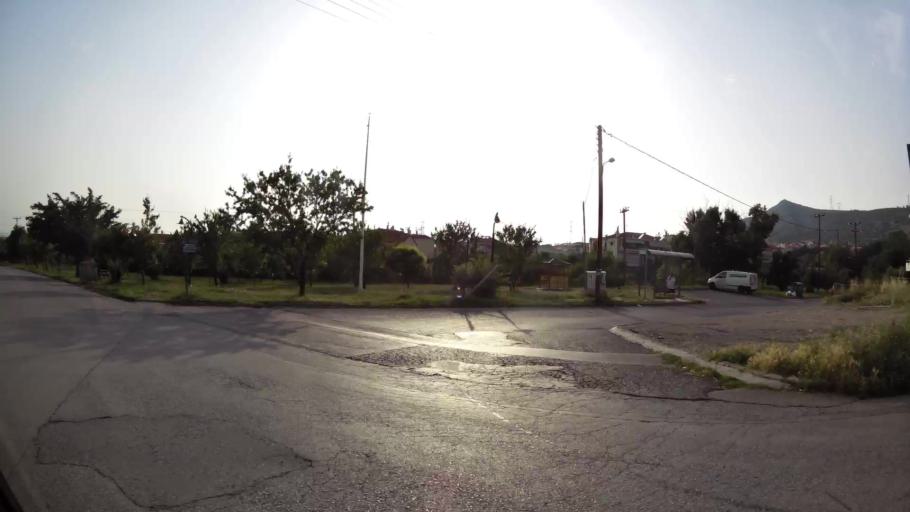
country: GR
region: Central Macedonia
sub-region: Nomos Thessalonikis
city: Oraiokastro
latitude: 40.7200
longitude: 22.9068
